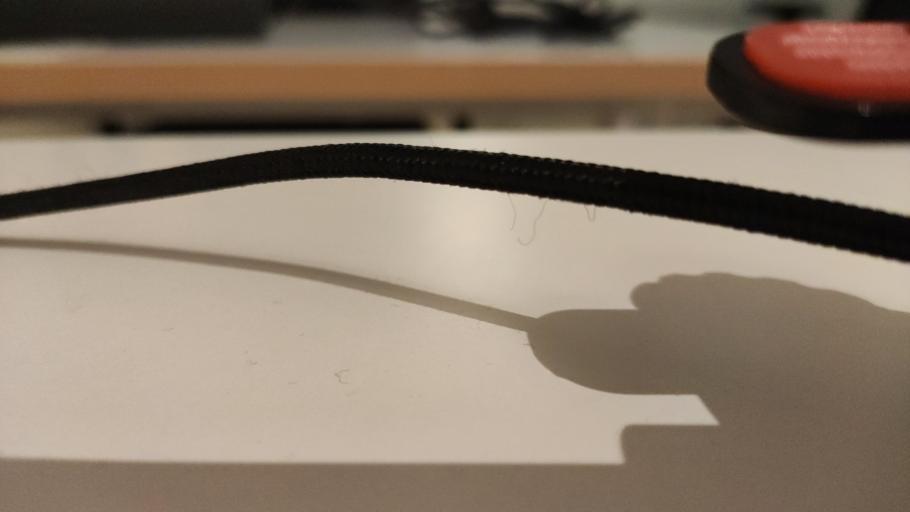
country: RU
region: Moskovskaya
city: Il'inskiy Pogost
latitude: 55.5245
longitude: 38.8721
